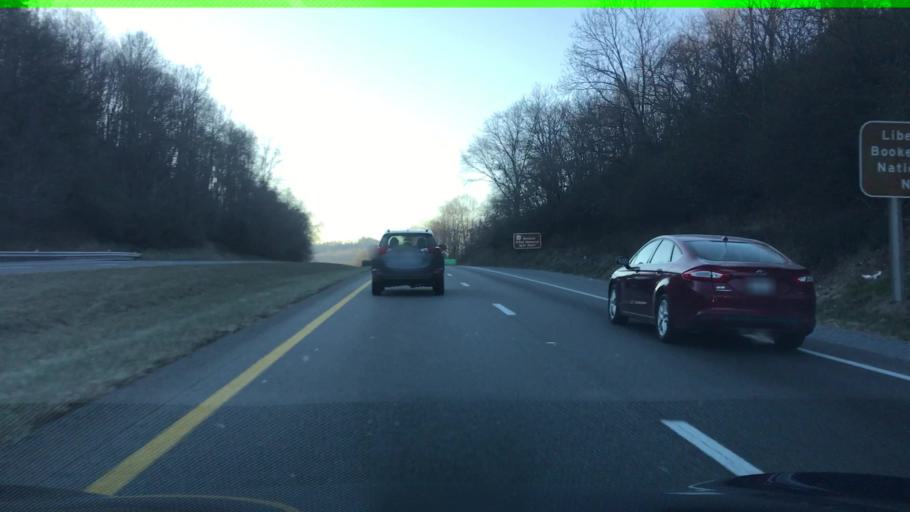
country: US
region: Virginia
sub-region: City of Bedford
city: Bedford
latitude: 37.3233
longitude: -79.5197
